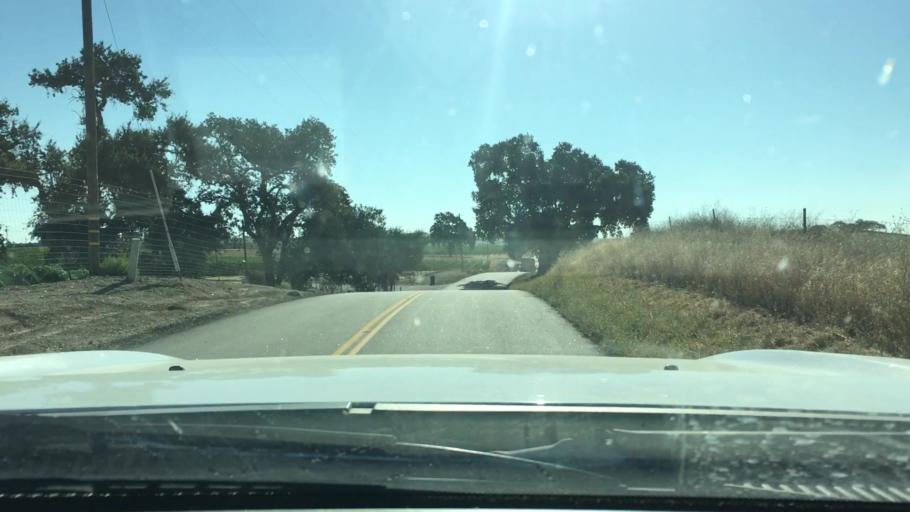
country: US
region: California
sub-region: San Luis Obispo County
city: Paso Robles
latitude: 35.5752
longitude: -120.6310
